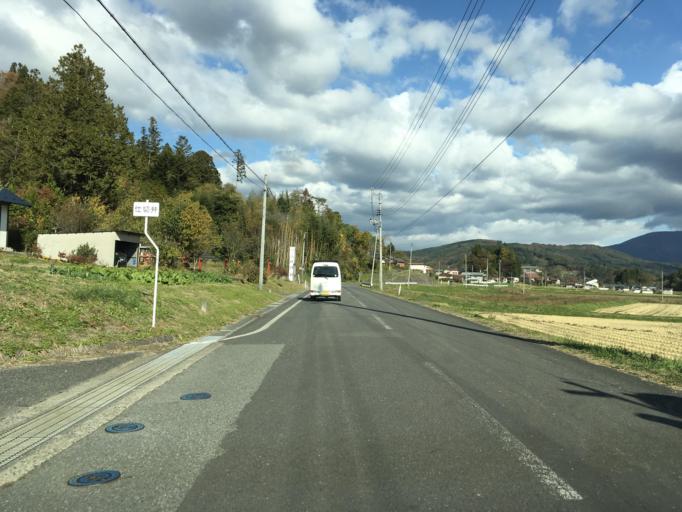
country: JP
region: Iwate
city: Ichinoseki
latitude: 38.9525
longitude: 141.3514
